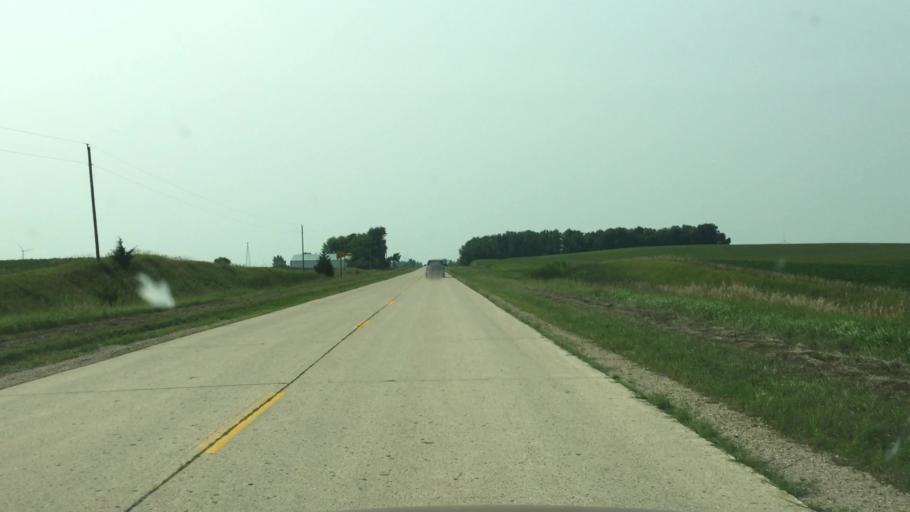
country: US
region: Iowa
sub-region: Dickinson County
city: Lake Park
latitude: 43.4242
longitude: -95.2891
